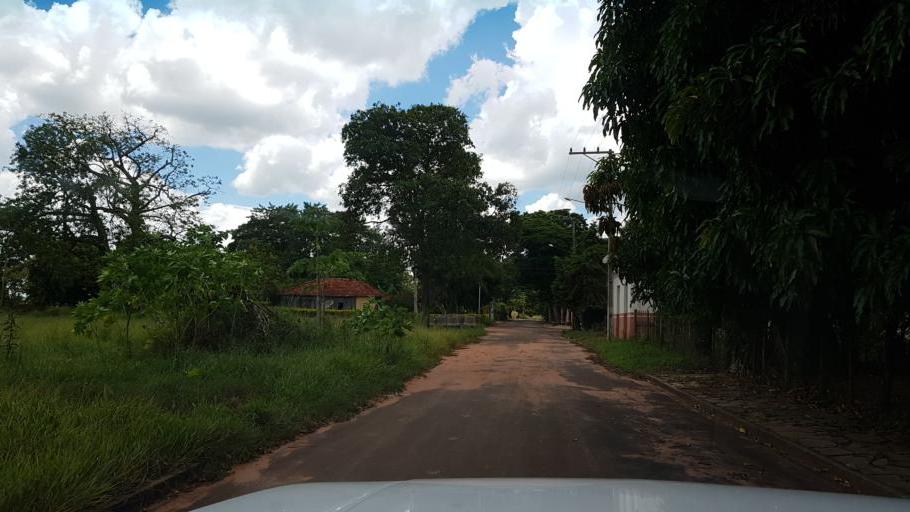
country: BR
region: Sao Paulo
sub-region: Paraguacu Paulista
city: Paraguacu Paulista
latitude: -22.3512
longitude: -50.6233
